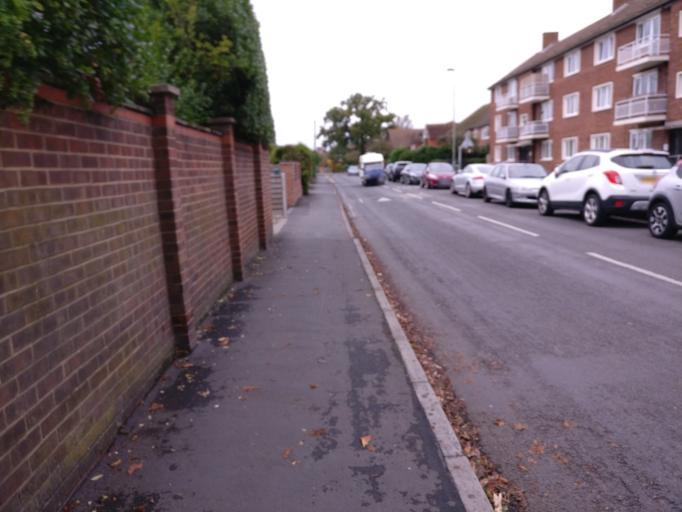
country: GB
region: England
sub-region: Surrey
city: Walton-on-Thames
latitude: 51.3826
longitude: -0.4072
